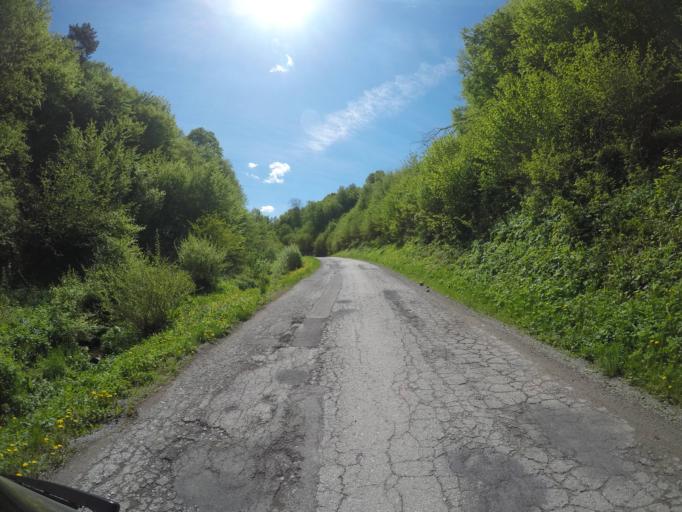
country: SK
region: Banskobystricky
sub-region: Okres Banska Bystrica
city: Banska Bystrica
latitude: 48.7234
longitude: 19.2183
